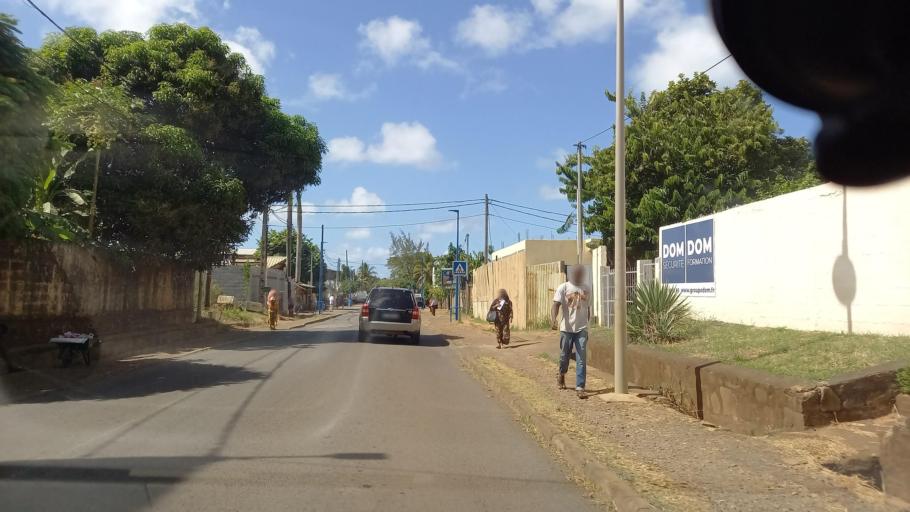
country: YT
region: Mamoudzou
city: Mamoudzou
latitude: -12.8010
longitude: 45.2073
